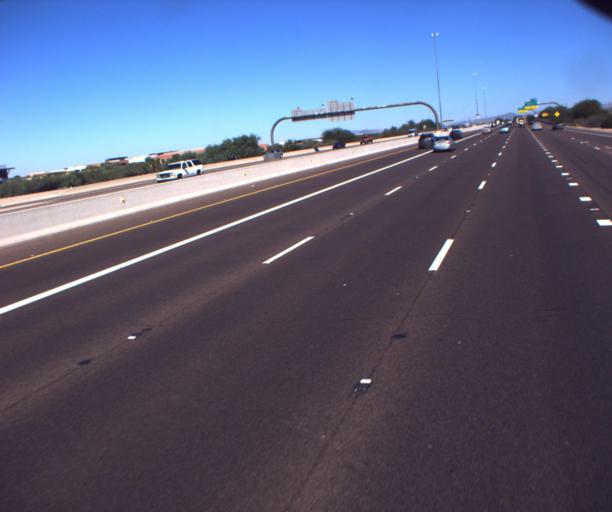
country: US
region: Arizona
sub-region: Maricopa County
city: Paradise Valley
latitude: 33.6362
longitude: -111.8902
